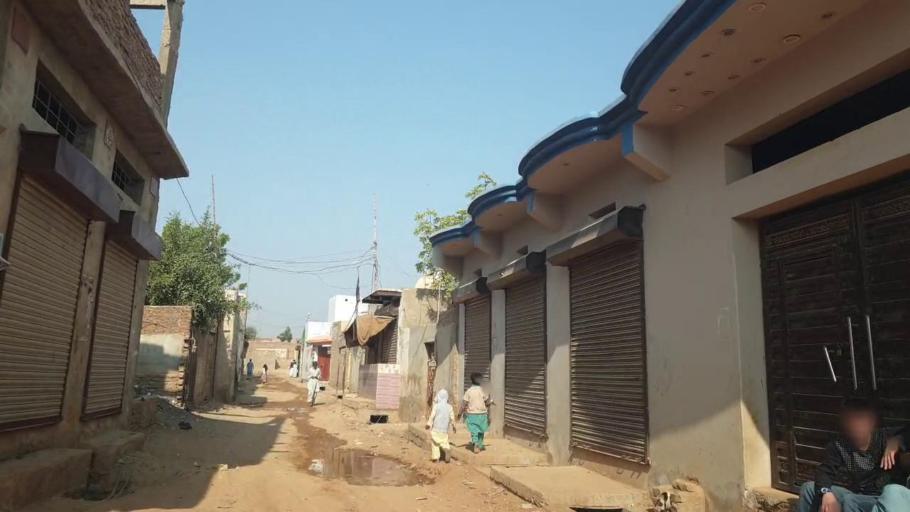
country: PK
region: Sindh
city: Jamshoro
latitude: 25.4347
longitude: 68.2806
